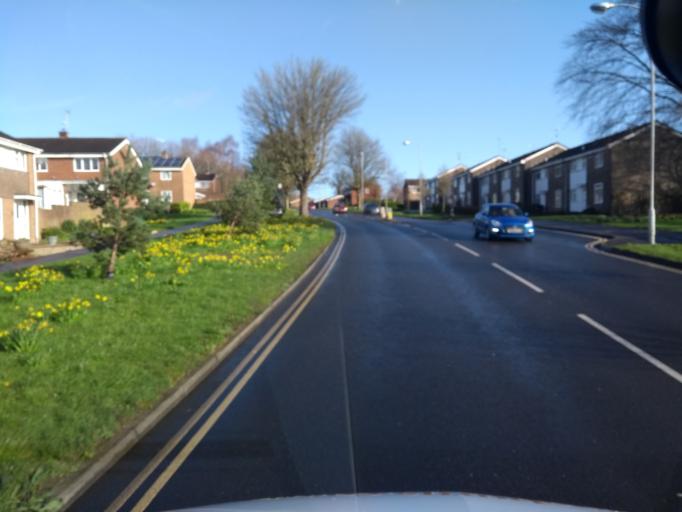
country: GB
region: England
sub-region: Somerset
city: Yeovil
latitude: 50.9498
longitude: -2.6084
